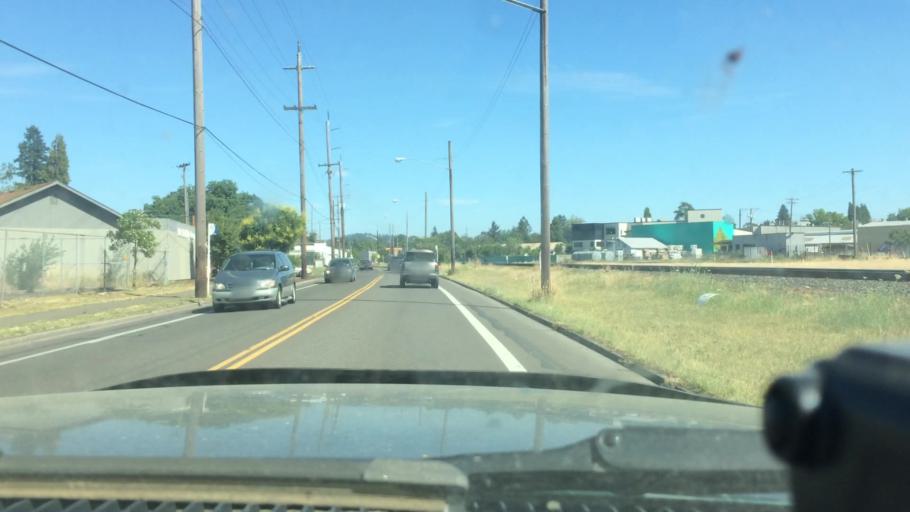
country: US
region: Oregon
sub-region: Lane County
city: Eugene
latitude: 44.0603
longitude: -123.1134
